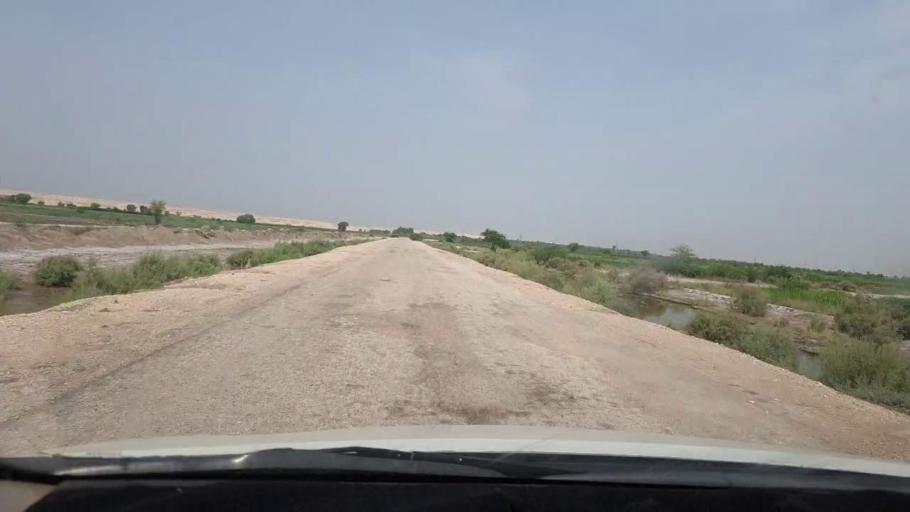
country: PK
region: Sindh
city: Rohri
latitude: 27.5952
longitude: 68.9941
